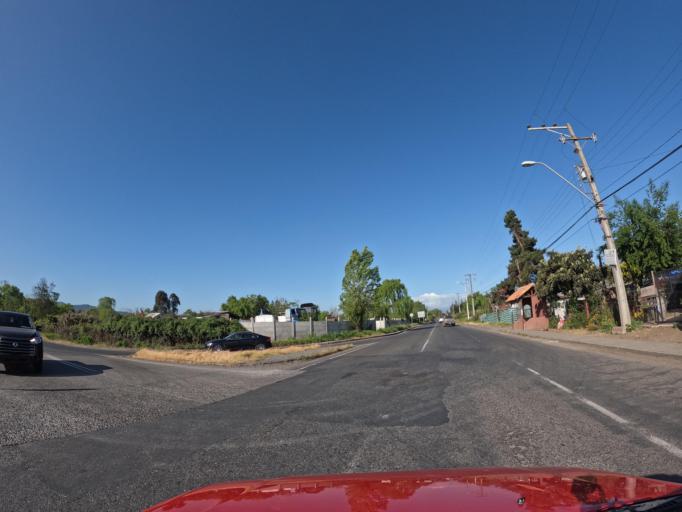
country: CL
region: Maule
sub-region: Provincia de Curico
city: Teno
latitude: -34.8597
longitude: -71.1910
